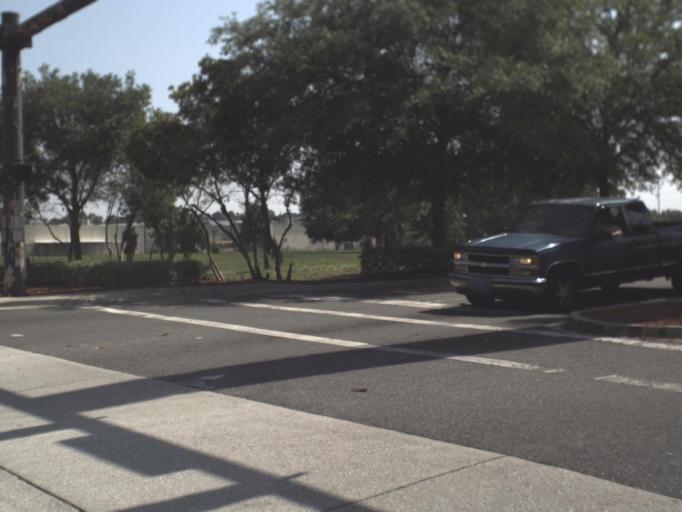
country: US
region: Florida
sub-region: Duval County
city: Jacksonville
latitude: 30.3111
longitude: -81.7519
